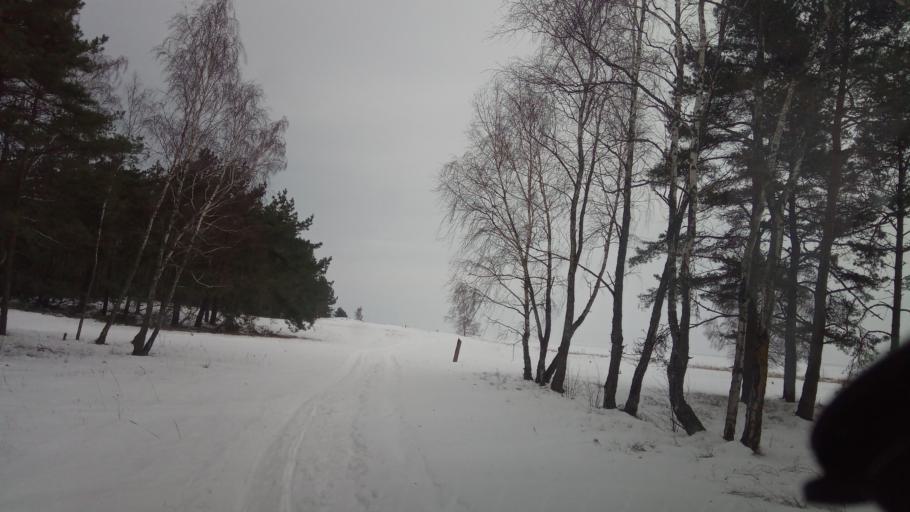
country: LT
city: Neringa
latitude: 55.4221
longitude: 21.1078
